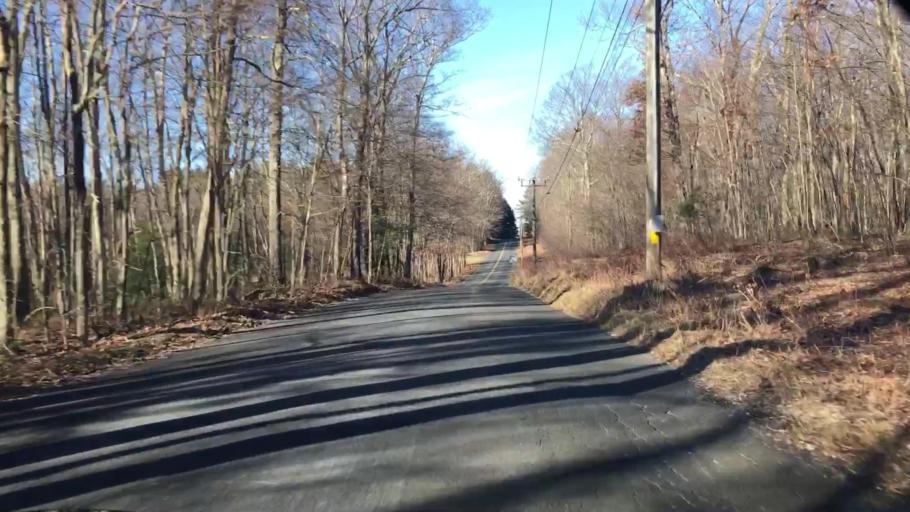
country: US
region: Connecticut
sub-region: Tolland County
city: Crystal Lake
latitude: 41.9592
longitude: -72.4061
